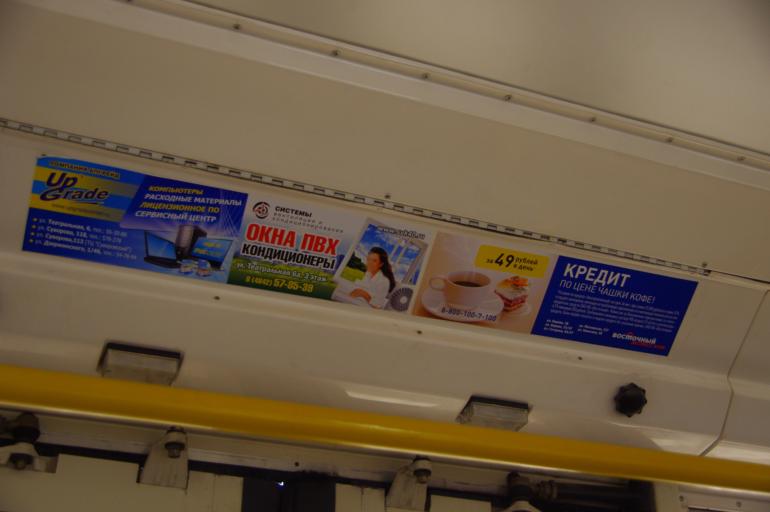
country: RU
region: Kaluga
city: Kaluga
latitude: 54.5130
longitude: 36.2406
